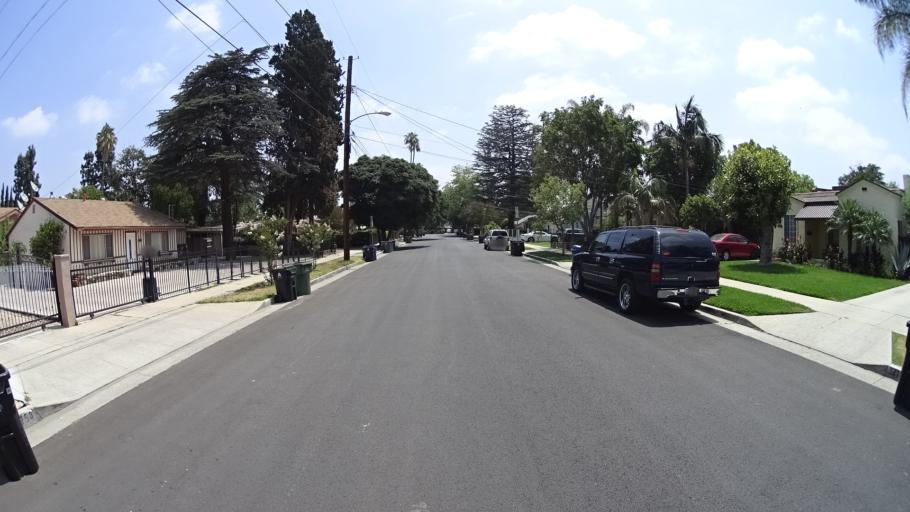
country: US
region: California
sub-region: Los Angeles County
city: Van Nuys
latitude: 34.1929
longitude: -118.4548
